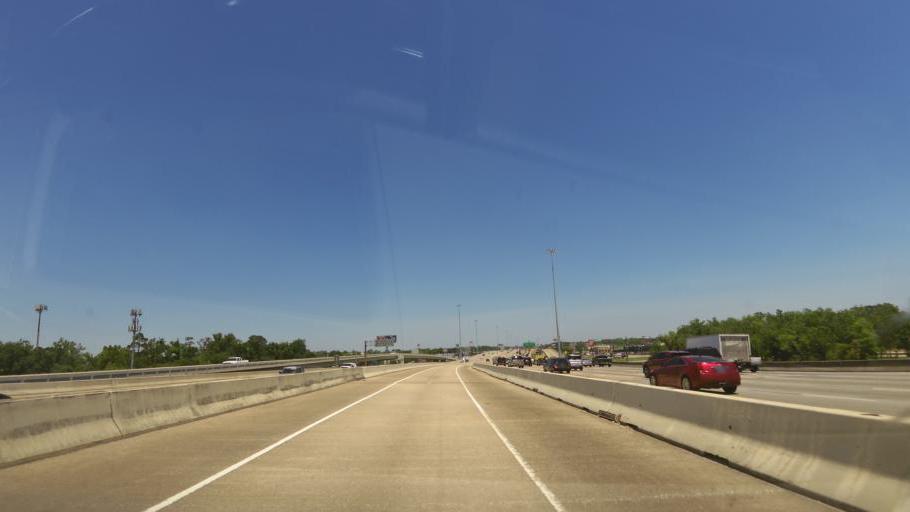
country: US
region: Texas
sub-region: Harris County
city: Aldine
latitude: 29.8646
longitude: -95.3330
